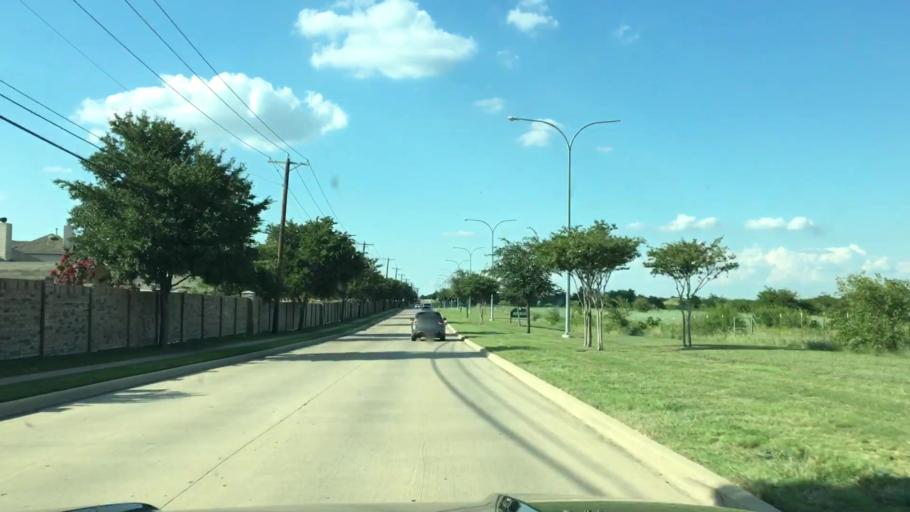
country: US
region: Texas
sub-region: Tarrant County
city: Haslet
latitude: 32.9742
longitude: -97.3816
